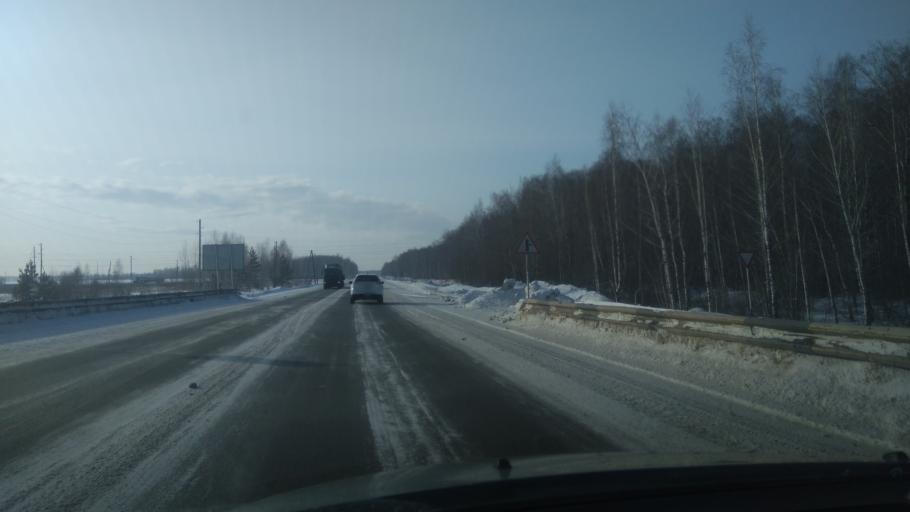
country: RU
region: Sverdlovsk
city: Bogdanovich
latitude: 56.8095
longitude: 62.0379
